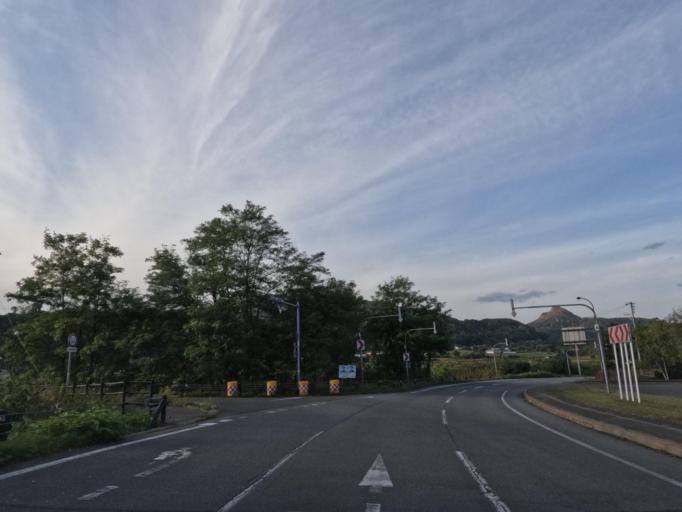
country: JP
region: Hokkaido
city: Date
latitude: 42.5089
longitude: 140.8615
